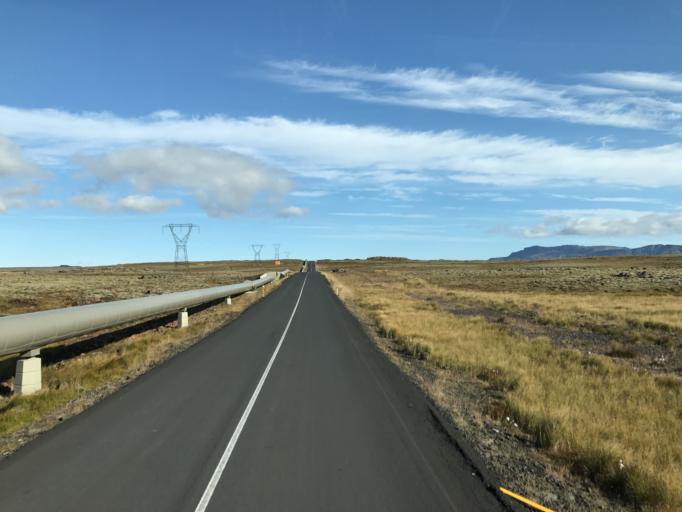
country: IS
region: Capital Region
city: Mosfellsbaer
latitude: 64.1104
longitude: -21.5566
